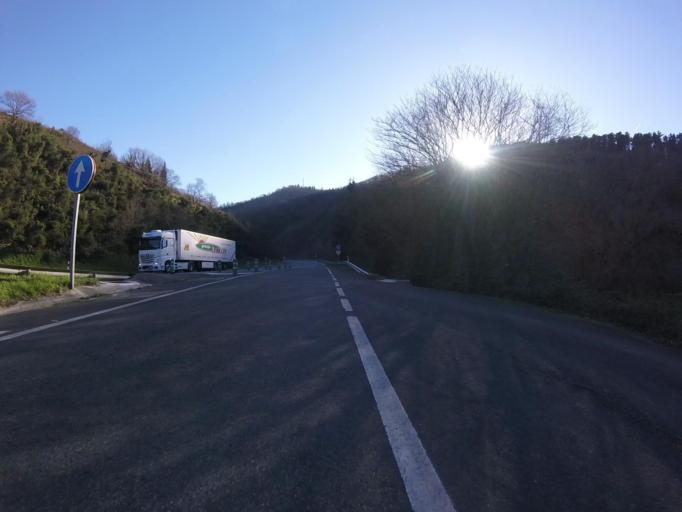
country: ES
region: Navarre
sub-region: Provincia de Navarra
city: Bera
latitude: 43.2649
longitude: -1.6852
